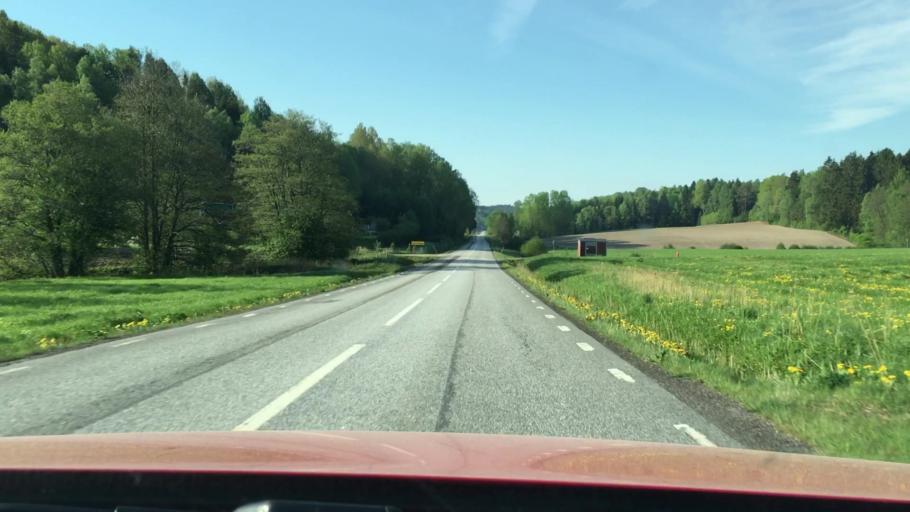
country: SE
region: Vaestra Goetaland
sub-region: Munkedals Kommun
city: Munkedal
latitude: 58.6189
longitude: 11.5584
